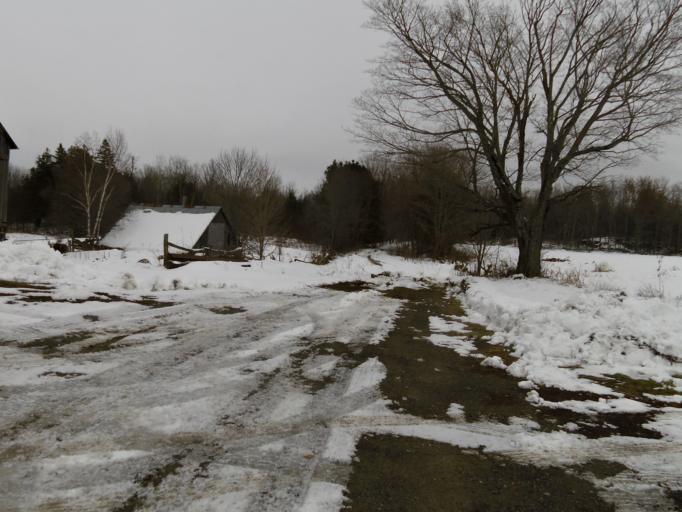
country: CA
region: Ontario
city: Carleton Place
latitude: 45.1152
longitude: -76.2449
